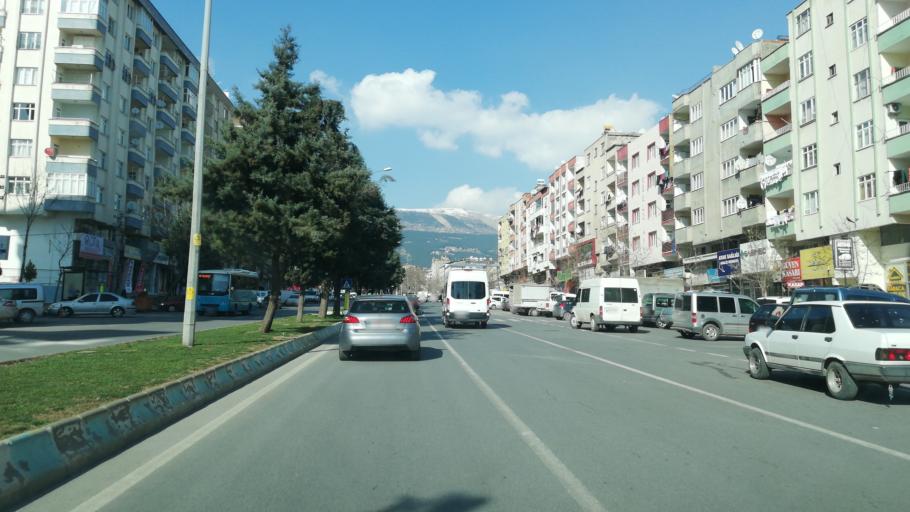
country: TR
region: Kahramanmaras
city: Kahramanmaras
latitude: 37.5761
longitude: 36.9232
